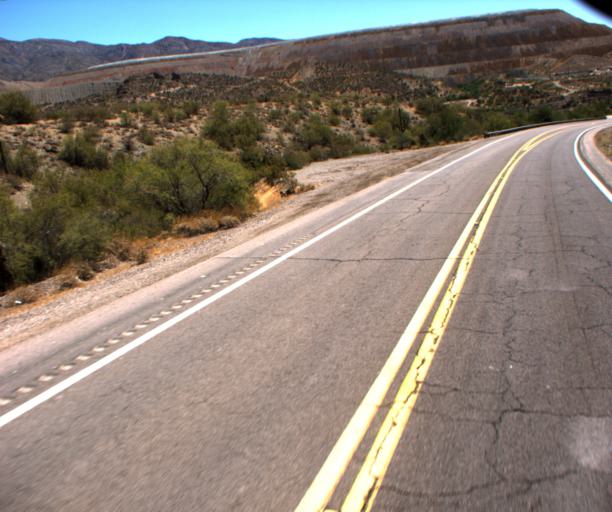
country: US
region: Arizona
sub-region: Pinal County
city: Kearny
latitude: 33.1303
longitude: -110.9826
